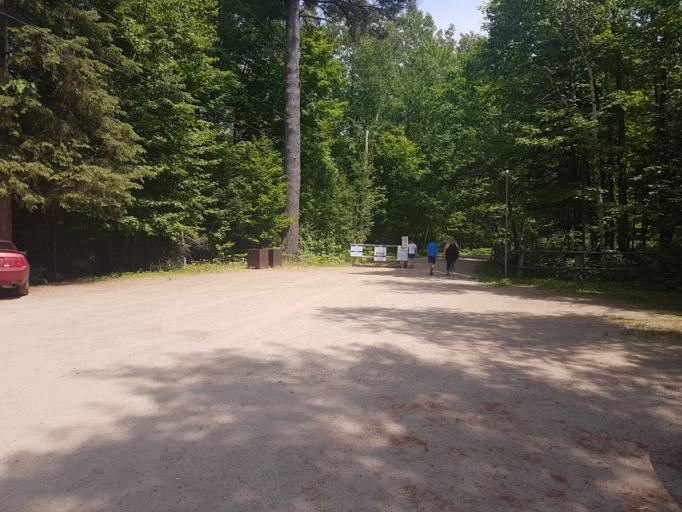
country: CA
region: Quebec
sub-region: Outaouais
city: Fort-Coulonge
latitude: 45.8760
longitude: -76.6884
